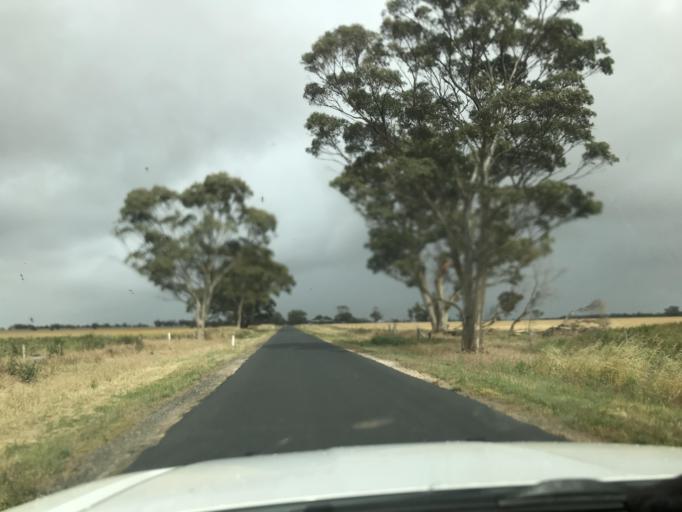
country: AU
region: South Australia
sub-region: Tatiara
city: Bordertown
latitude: -36.3444
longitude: 141.2322
